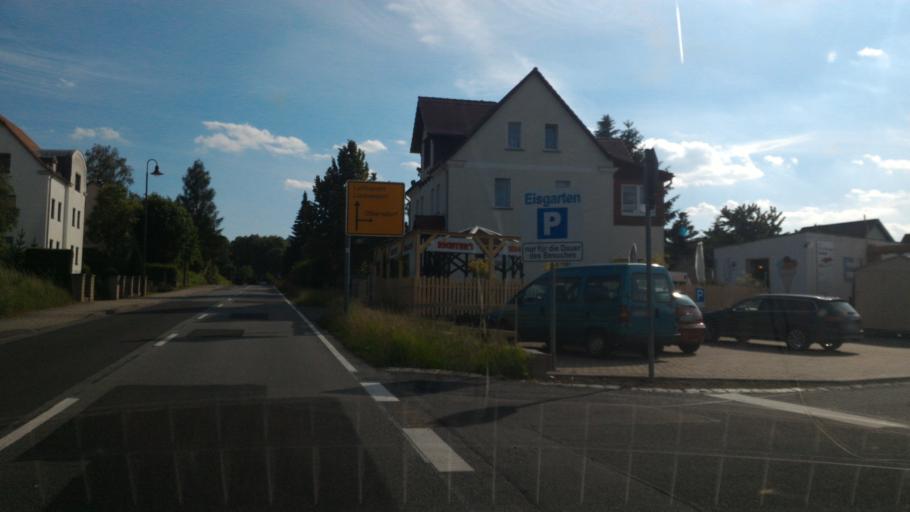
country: DE
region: Saxony
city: Olbersdorf
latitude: 50.8608
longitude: 14.7965
